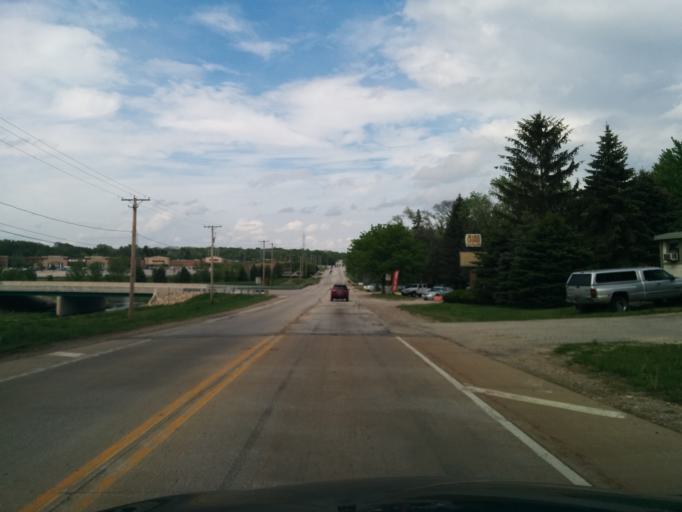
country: US
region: Illinois
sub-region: Cook County
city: Lemont
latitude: 41.6401
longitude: -88.0051
